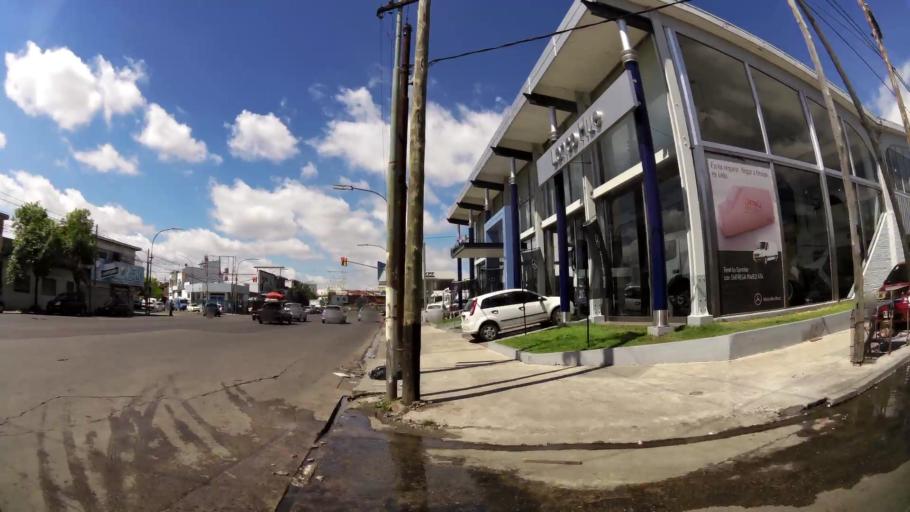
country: AR
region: Buenos Aires
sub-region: Partido de Lanus
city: Lanus
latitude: -34.6674
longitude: -58.4175
